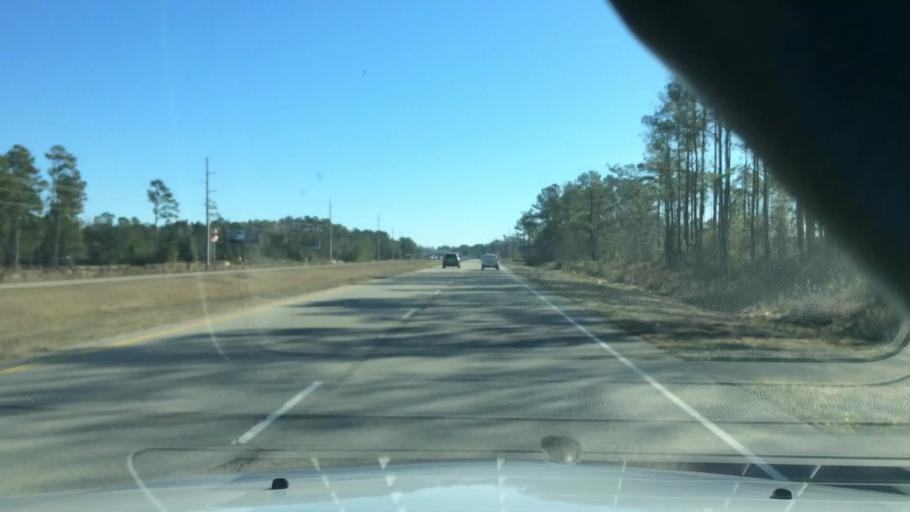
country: US
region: North Carolina
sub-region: Brunswick County
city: Shallotte
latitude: 33.9875
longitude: -78.3709
